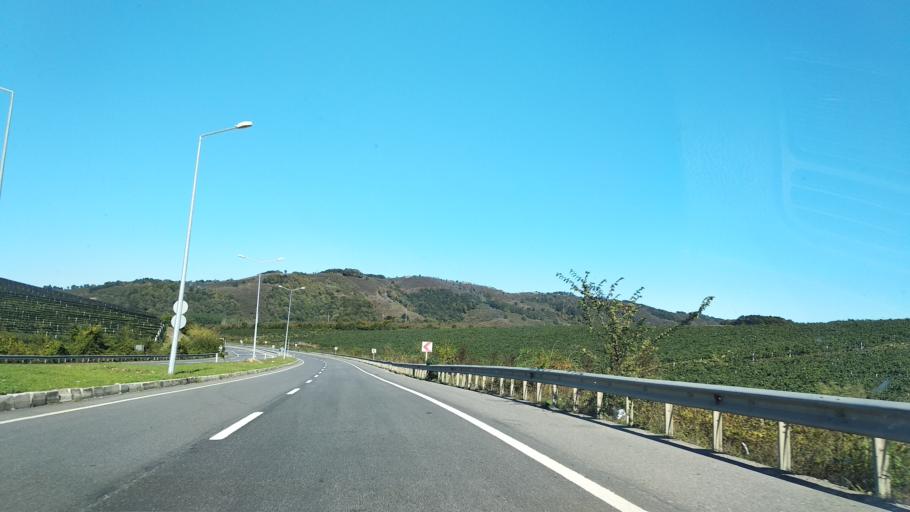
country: TR
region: Sakarya
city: Karasu
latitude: 41.0482
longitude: 30.6316
